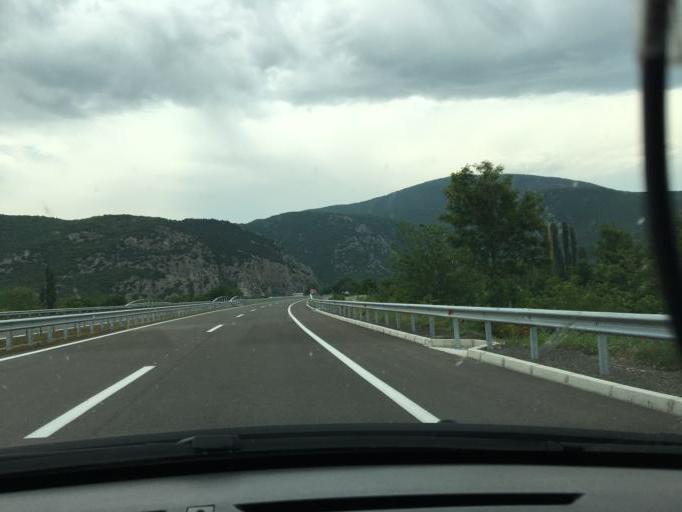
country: MK
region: Demir Kapija
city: Demir Kapija
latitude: 41.4143
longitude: 22.2426
